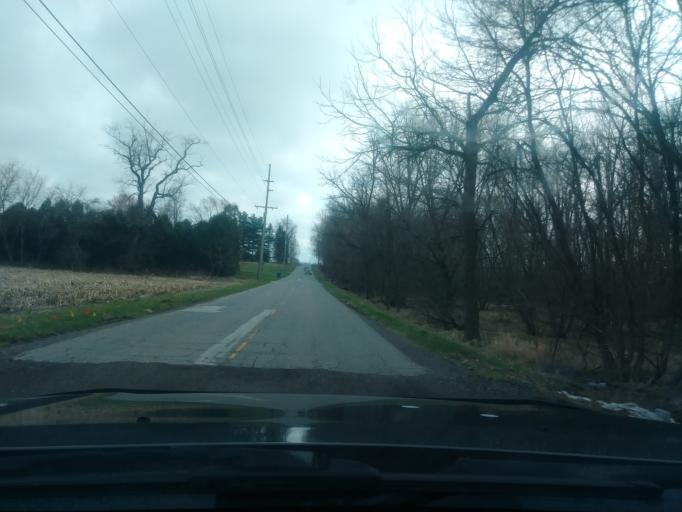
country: US
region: Indiana
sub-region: LaPorte County
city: LaPorte
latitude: 41.6239
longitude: -86.7965
